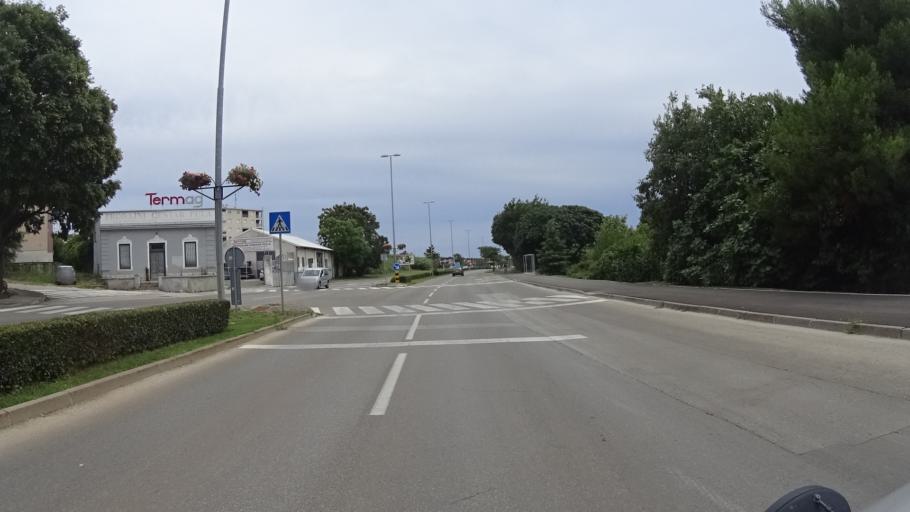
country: HR
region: Istarska
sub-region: Grad Pula
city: Pula
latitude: 44.8512
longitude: 13.8408
